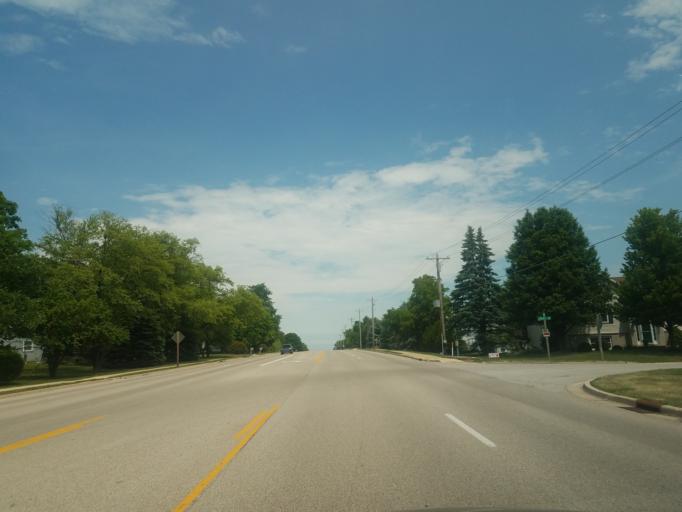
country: US
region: Illinois
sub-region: McLean County
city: Downs
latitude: 40.4202
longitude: -88.9013
